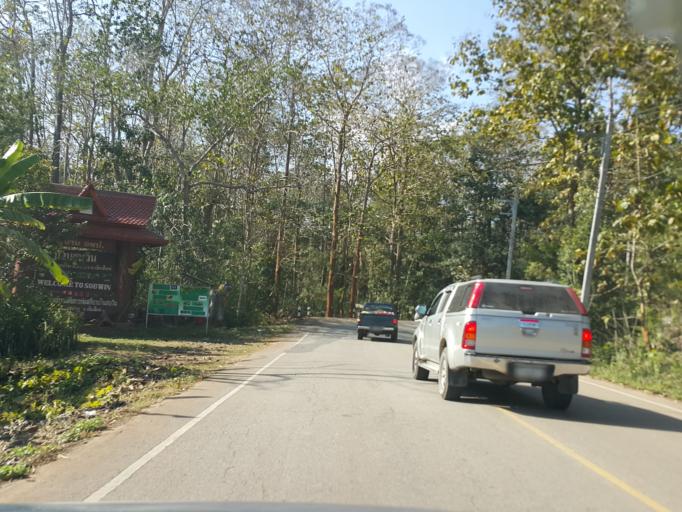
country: TH
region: Chiang Mai
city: Mae Wang
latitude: 18.6489
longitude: 98.6924
